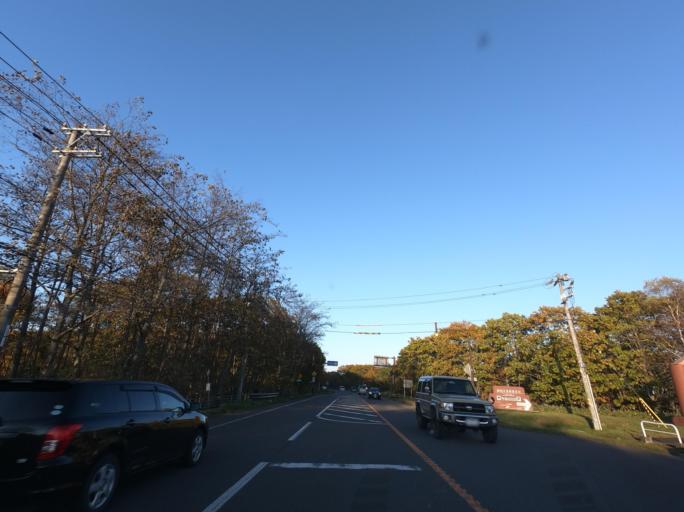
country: JP
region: Hokkaido
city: Kushiro
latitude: 43.0745
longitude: 144.3201
